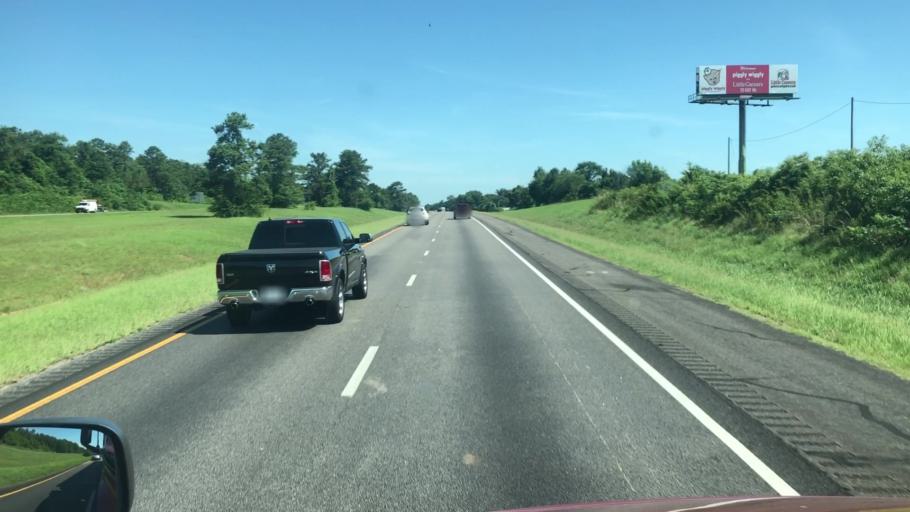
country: US
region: Alabama
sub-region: Autauga County
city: Pine Level
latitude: 32.5628
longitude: -86.4635
